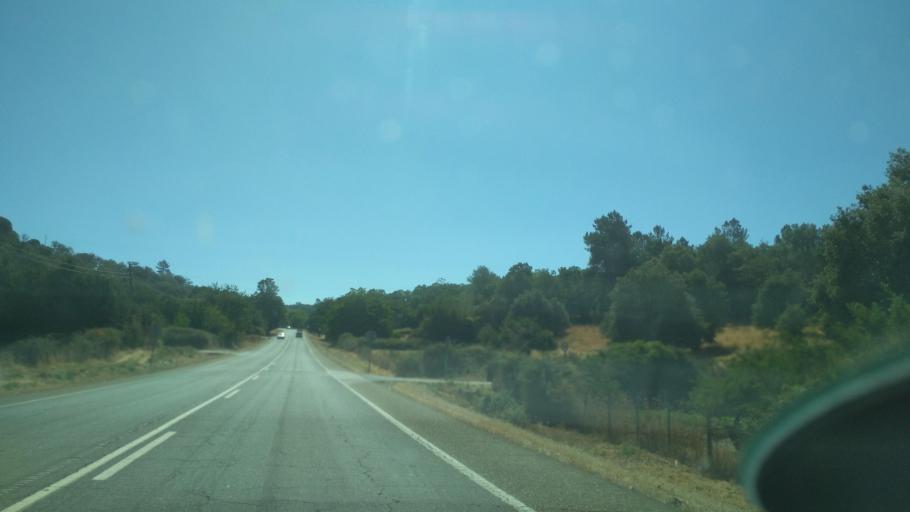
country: ES
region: Andalusia
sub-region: Provincia de Huelva
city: Galaroza
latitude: 37.9213
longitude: -6.6987
